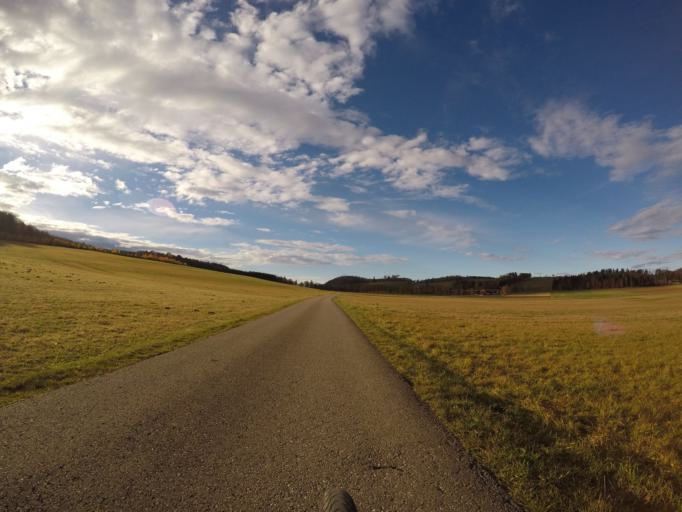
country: DE
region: Baden-Wuerttemberg
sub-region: Tuebingen Region
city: Sankt Johann
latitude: 48.4691
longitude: 9.3095
